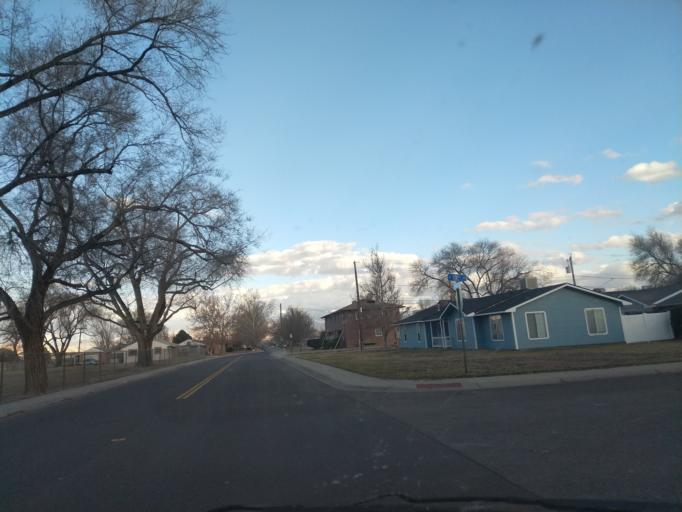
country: US
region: Colorado
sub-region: Mesa County
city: Grand Junction
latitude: 39.0734
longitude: -108.5444
